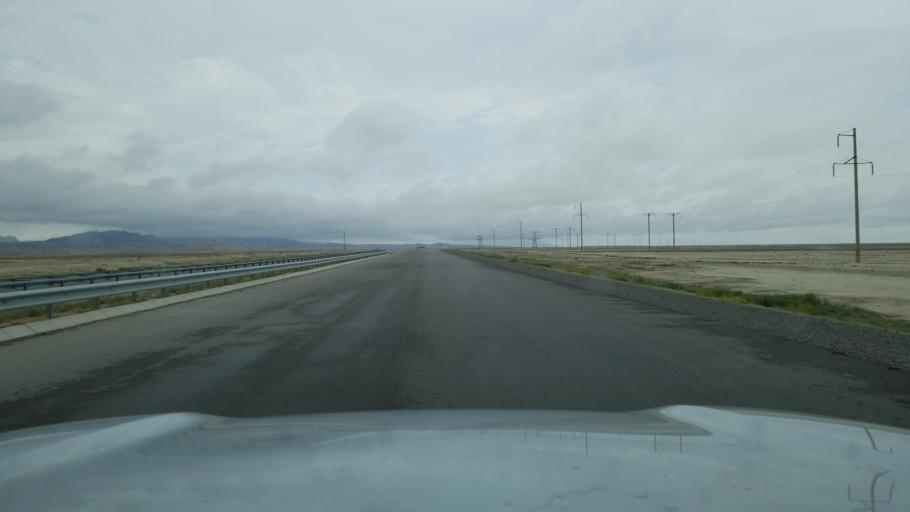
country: TM
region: Balkan
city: Serdar
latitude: 39.1032
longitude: 55.9460
